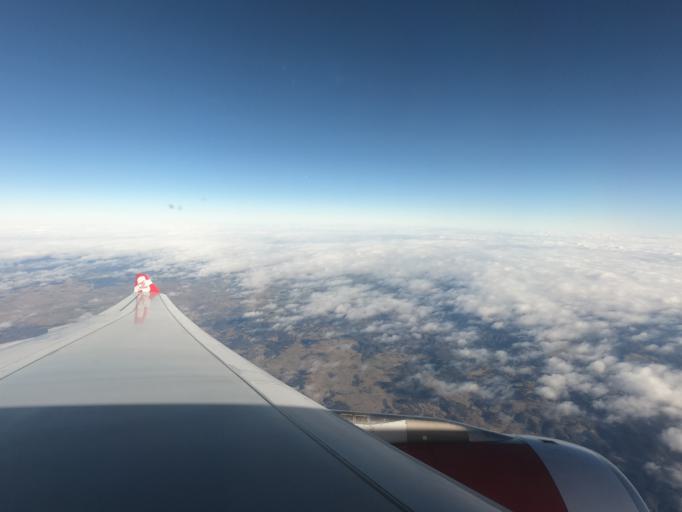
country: AU
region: New South Wales
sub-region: Wingecarribee
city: Bundanoon
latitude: -34.4396
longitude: 150.0327
